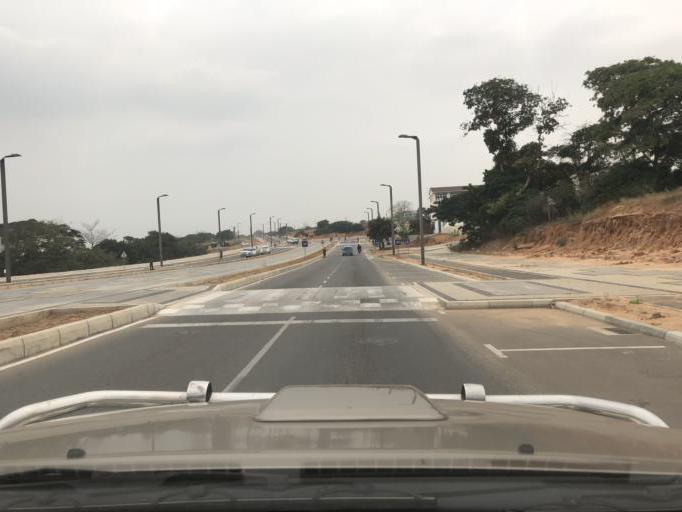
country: AO
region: Luanda
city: Luanda
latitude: -8.9007
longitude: 13.1746
